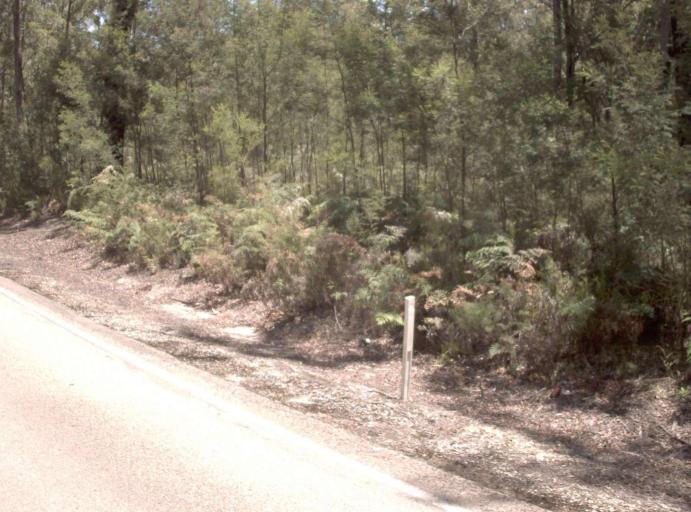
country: AU
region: Victoria
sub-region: East Gippsland
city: Lakes Entrance
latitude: -37.6502
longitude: 147.8917
